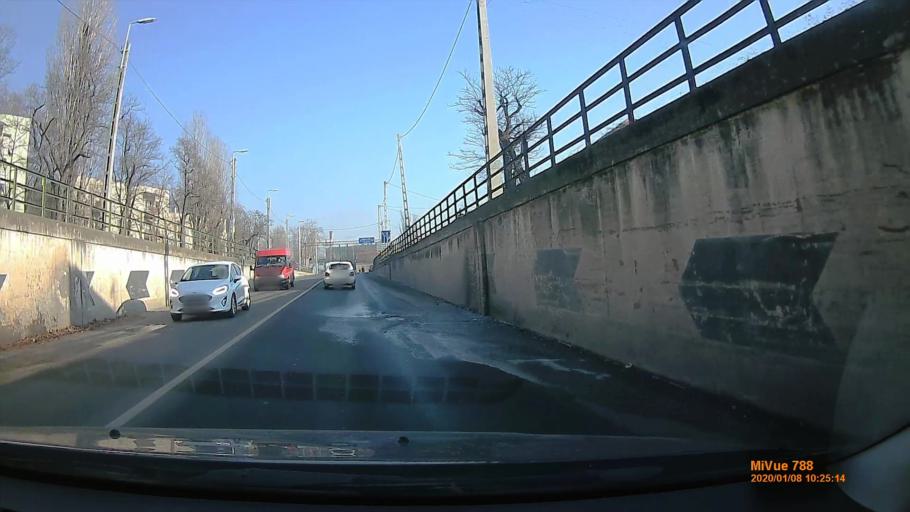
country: HU
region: Bacs-Kiskun
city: Kecskemet
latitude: 46.9109
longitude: 19.7057
